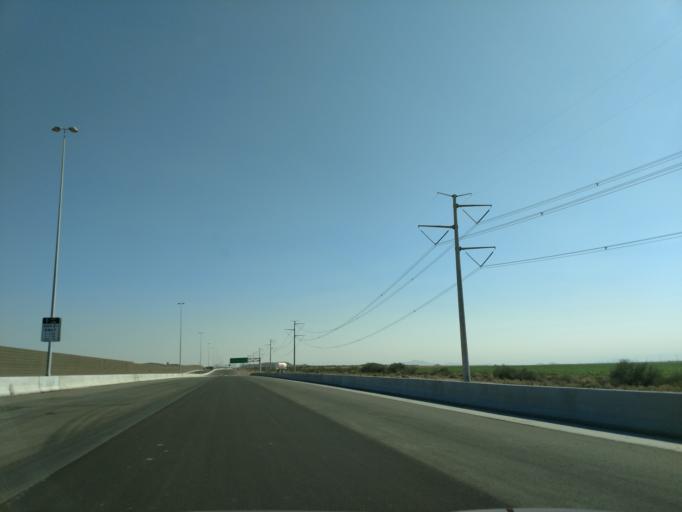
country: US
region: Arizona
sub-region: Maricopa County
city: Laveen
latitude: 33.2910
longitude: -112.1237
